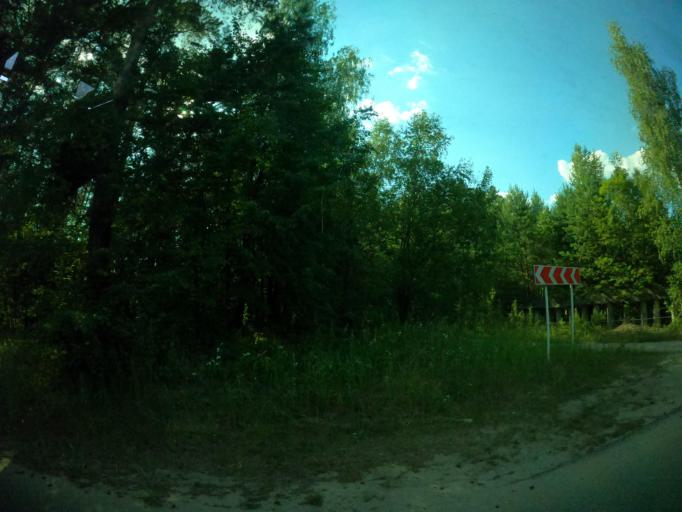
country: RU
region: Moskovskaya
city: Protvino
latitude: 54.8667
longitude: 37.1964
